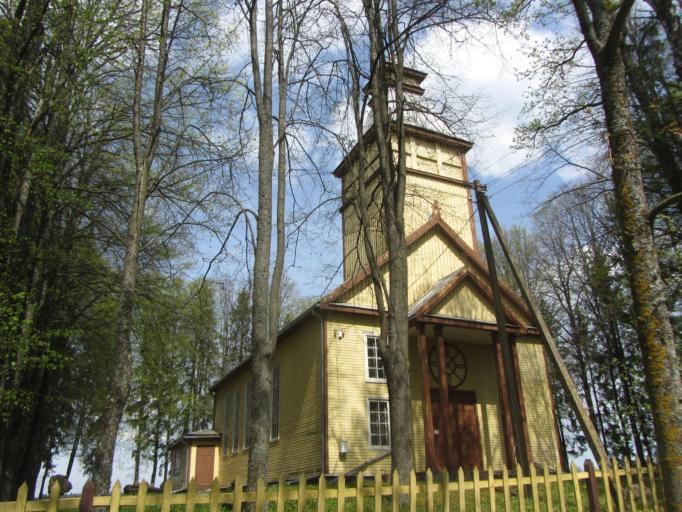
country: LT
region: Utenos apskritis
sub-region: Anyksciai
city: Anyksciai
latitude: 55.4320
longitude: 25.1737
